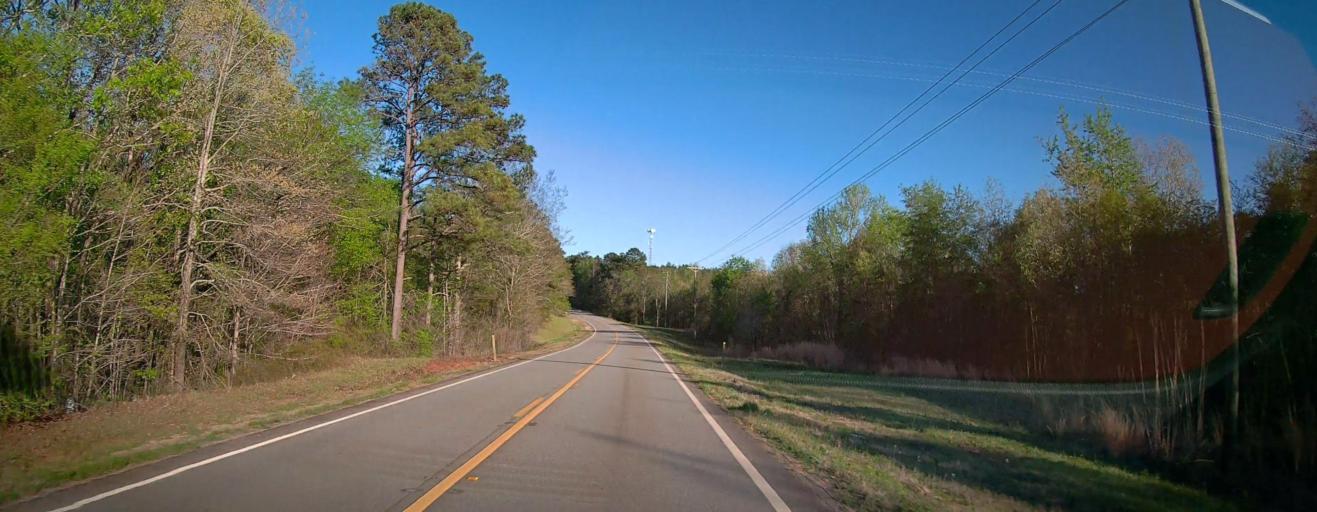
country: US
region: Georgia
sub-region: Wilkinson County
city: Irwinton
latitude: 32.8594
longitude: -83.0794
